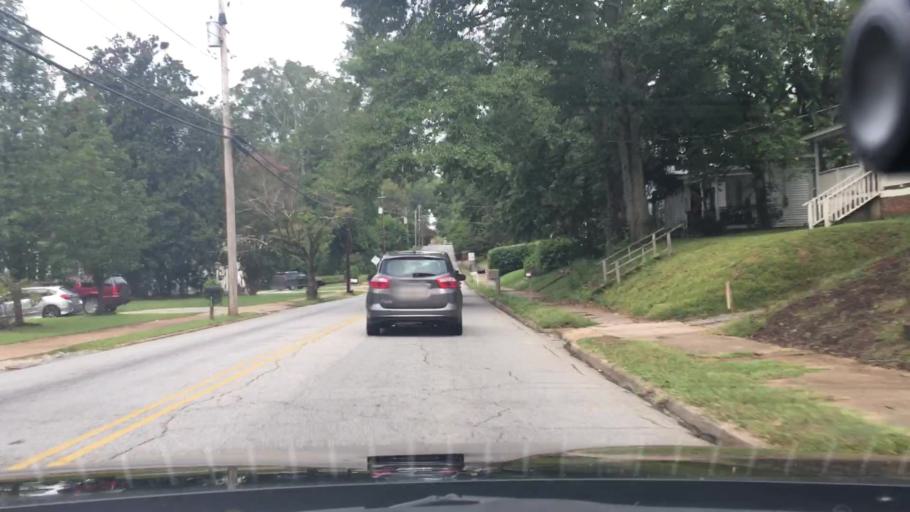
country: US
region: Georgia
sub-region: Coweta County
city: Newnan
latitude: 33.3738
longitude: -84.7912
